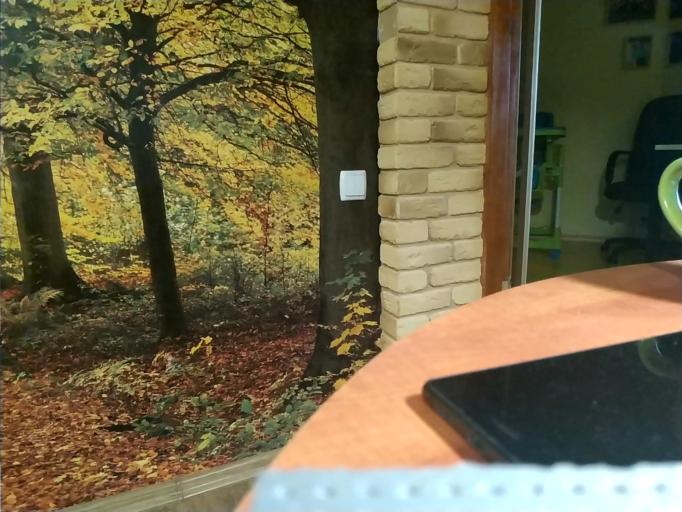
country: RU
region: Moskovskaya
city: Klin
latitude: 56.3426
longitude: 36.7463
